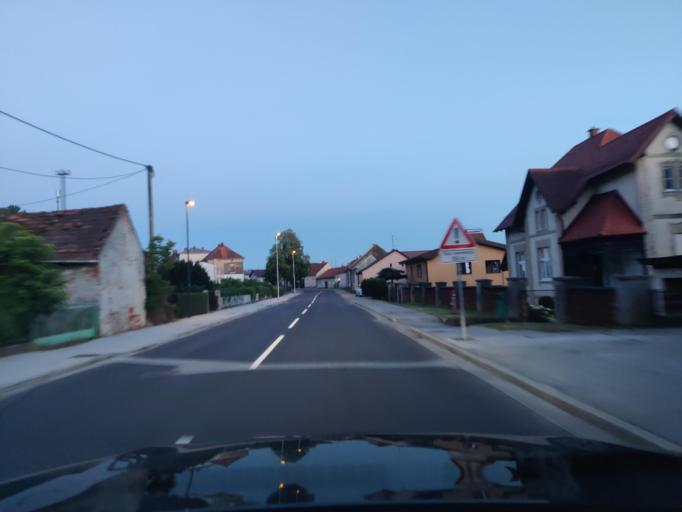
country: SI
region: Lendava-Lendva
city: Lendava
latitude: 46.5715
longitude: 16.4481
